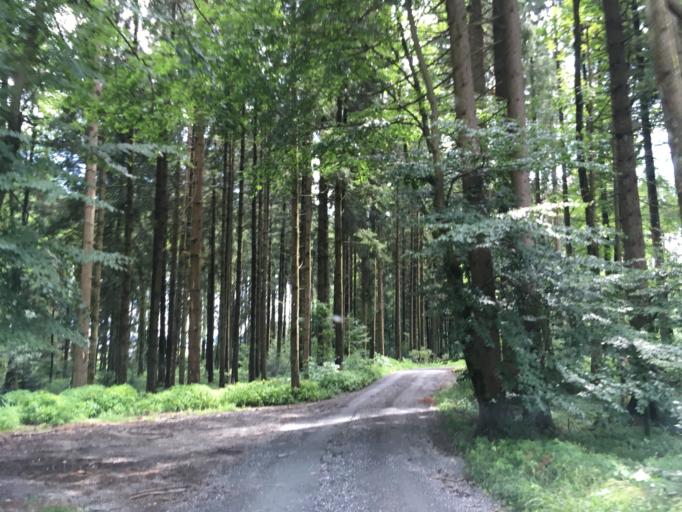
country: DE
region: Bavaria
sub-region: Upper Bavaria
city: Pittenhart
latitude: 48.0076
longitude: 12.3630
